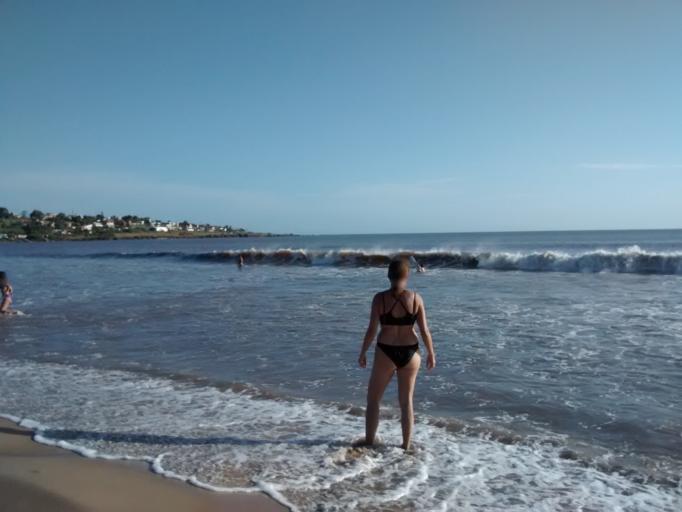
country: UY
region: Maldonado
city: Piriapolis
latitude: -34.8933
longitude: -55.2624
